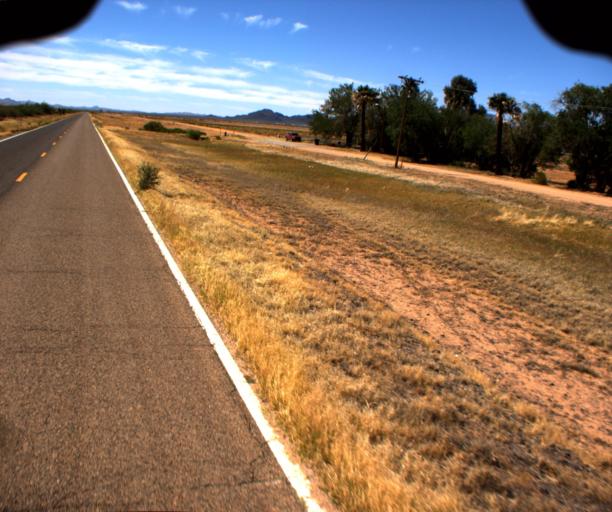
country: US
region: Arizona
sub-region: Yavapai County
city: Congress
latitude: 33.9695
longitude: -113.1416
